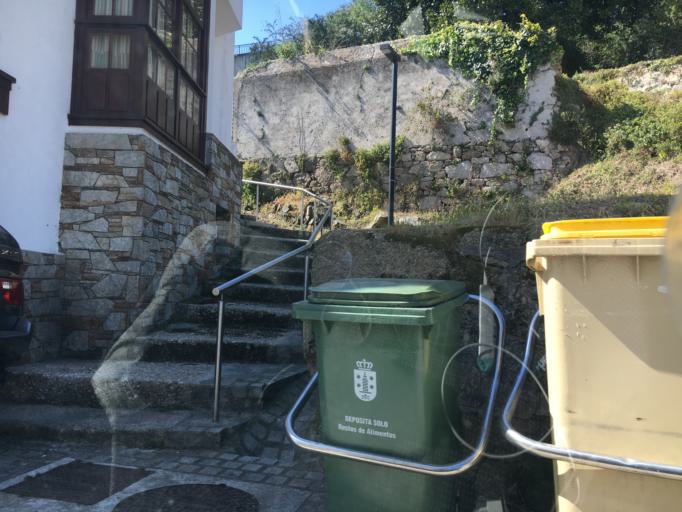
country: ES
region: Galicia
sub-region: Provincia da Coruna
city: A Coruna
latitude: 43.3422
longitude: -8.3870
